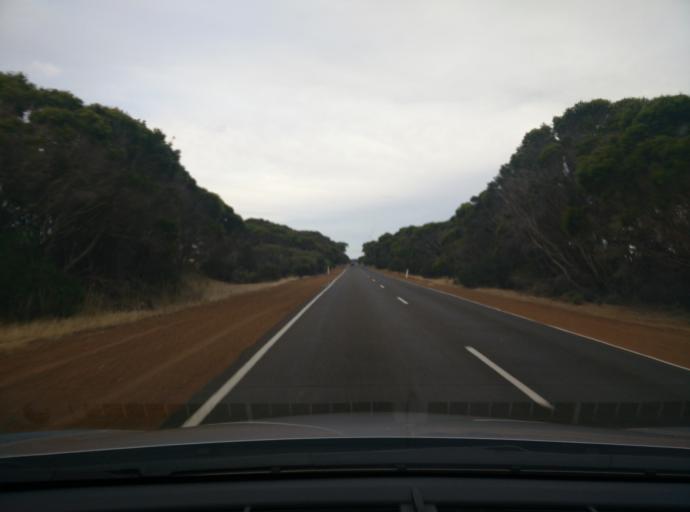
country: AU
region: South Australia
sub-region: Kangaroo Island
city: Kingscote
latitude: -35.7119
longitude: 137.5632
